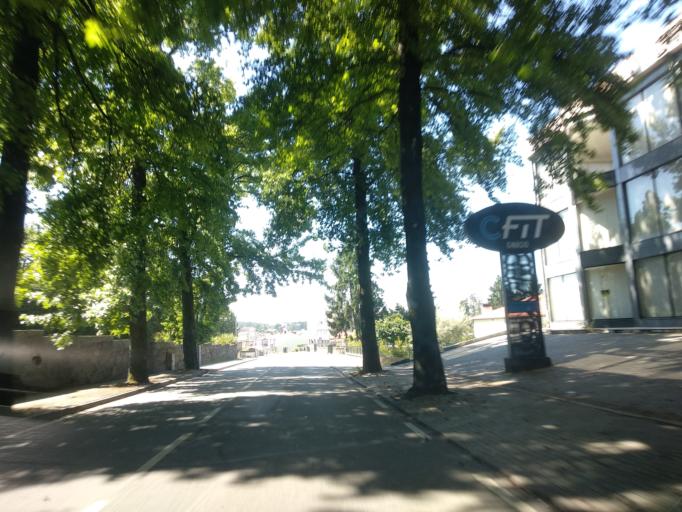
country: PT
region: Porto
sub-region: Pacos de Ferreira
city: Freamunde
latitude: 41.2843
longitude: -8.3339
